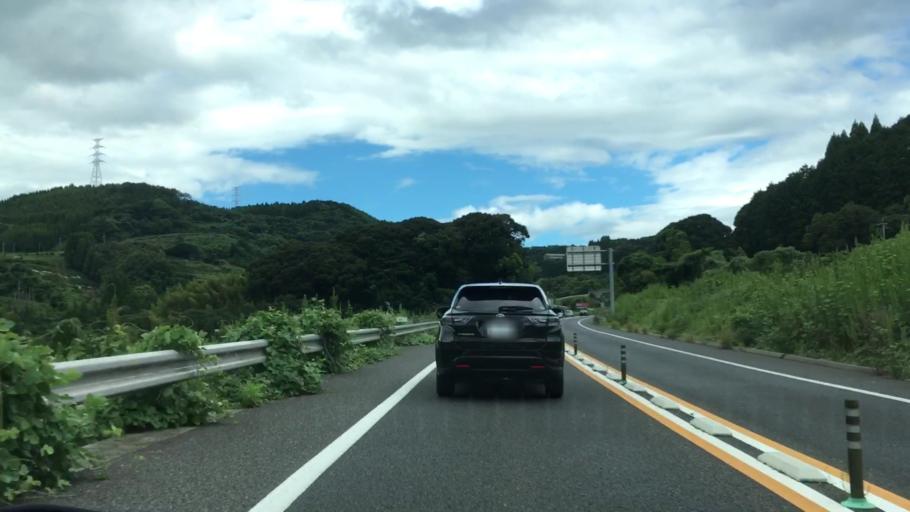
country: JP
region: Saga Prefecture
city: Karatsu
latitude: 33.3941
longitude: 129.9350
